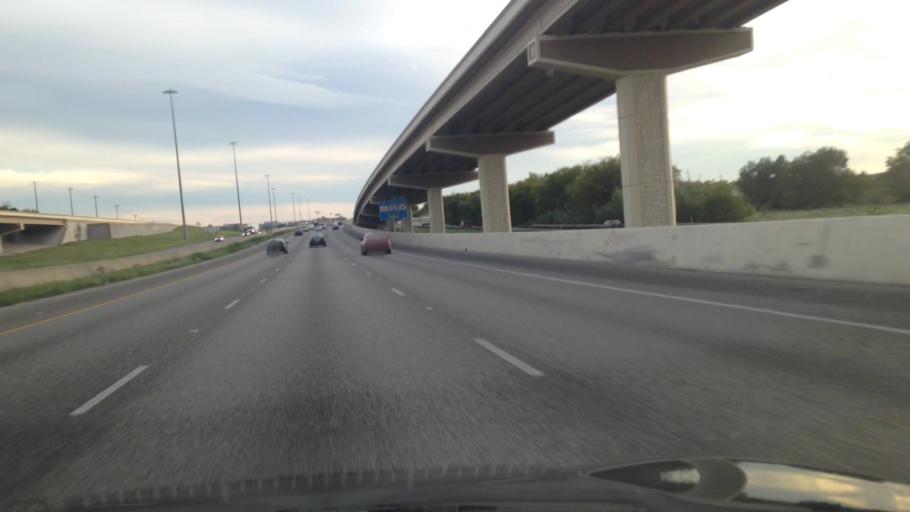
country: US
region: Texas
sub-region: Travis County
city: Onion Creek
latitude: 30.1081
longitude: -97.8091
